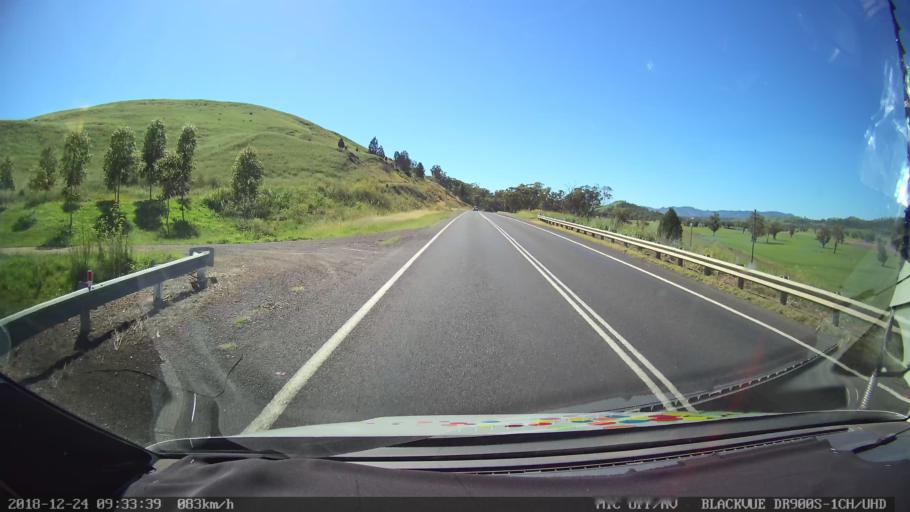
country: AU
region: New South Wales
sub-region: Liverpool Plains
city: Quirindi
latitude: -31.6057
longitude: 150.7094
